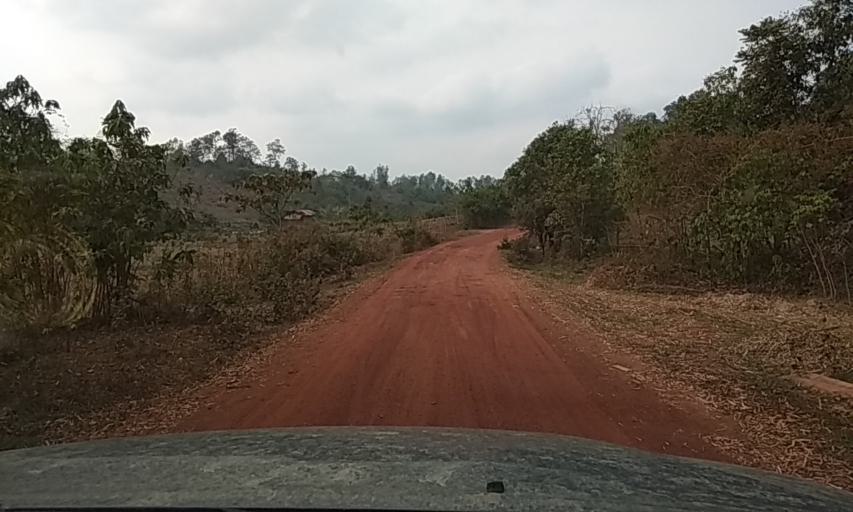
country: TH
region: Nan
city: Mae Charim
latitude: 18.4134
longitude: 101.1734
